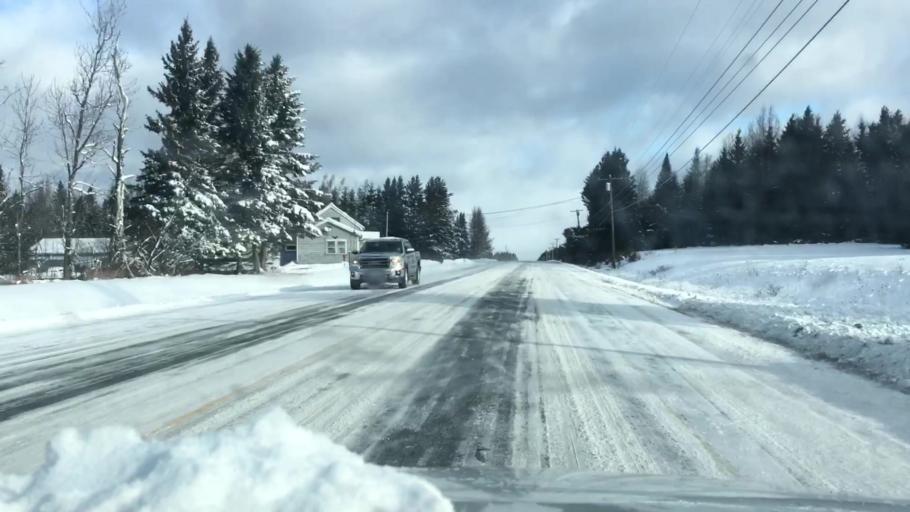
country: US
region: Maine
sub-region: Aroostook County
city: Madawaska
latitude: 47.0070
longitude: -68.0219
